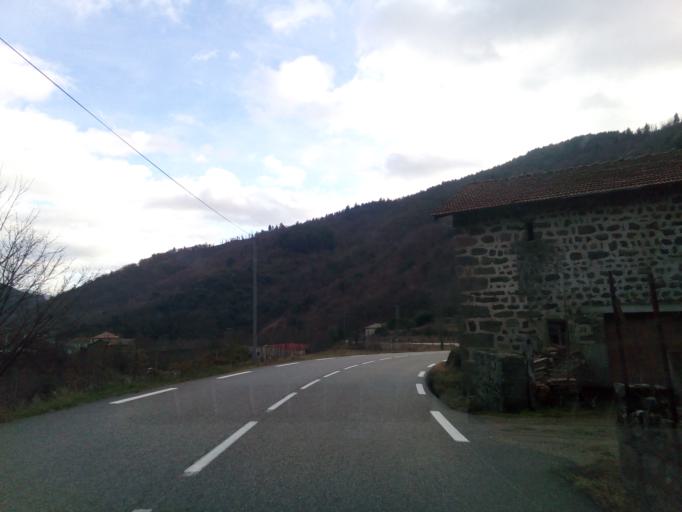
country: FR
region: Rhone-Alpes
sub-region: Departement de l'Ardeche
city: Saint-Sauveur-de-Montagut
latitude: 44.8763
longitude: 4.5368
